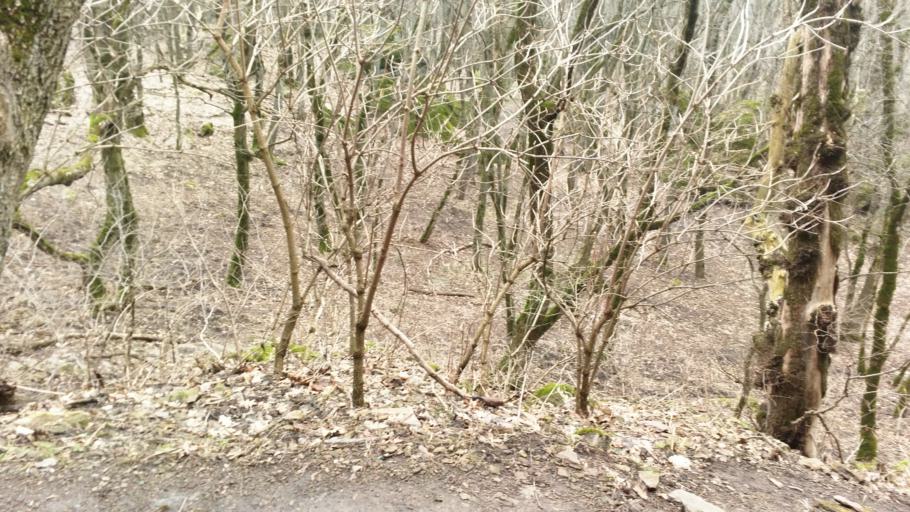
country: RU
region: Stavropol'skiy
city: Zheleznovodsk
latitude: 44.1563
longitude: 43.0450
